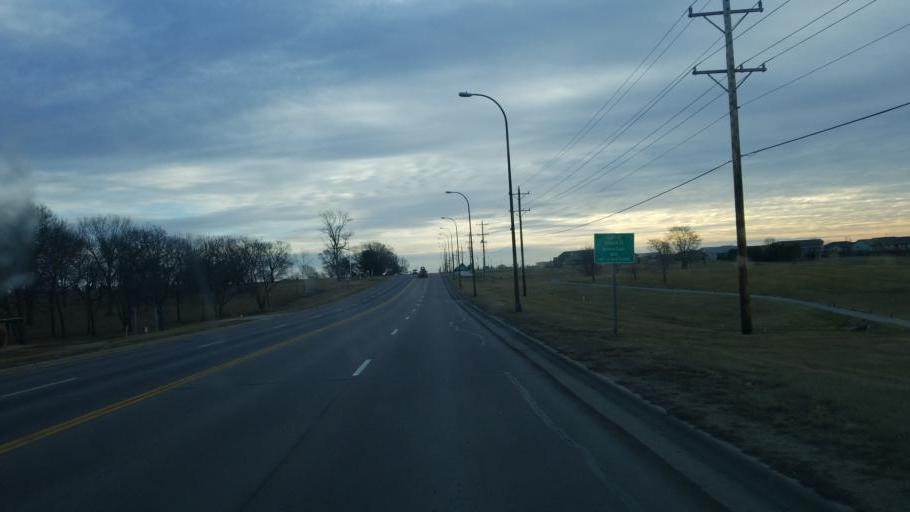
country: US
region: South Dakota
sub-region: Yankton County
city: Yankton
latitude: 42.9088
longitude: -97.4067
